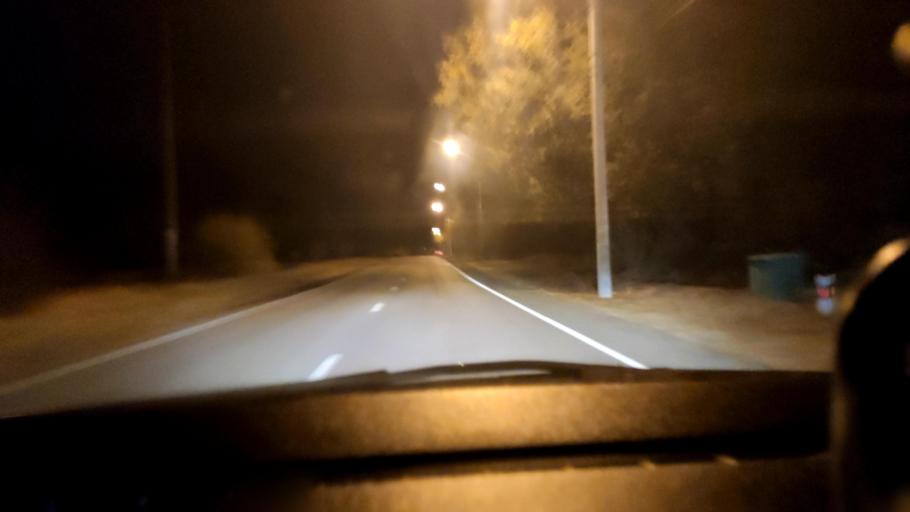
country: RU
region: Voronezj
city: Pridonskoy
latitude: 51.6132
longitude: 39.0526
